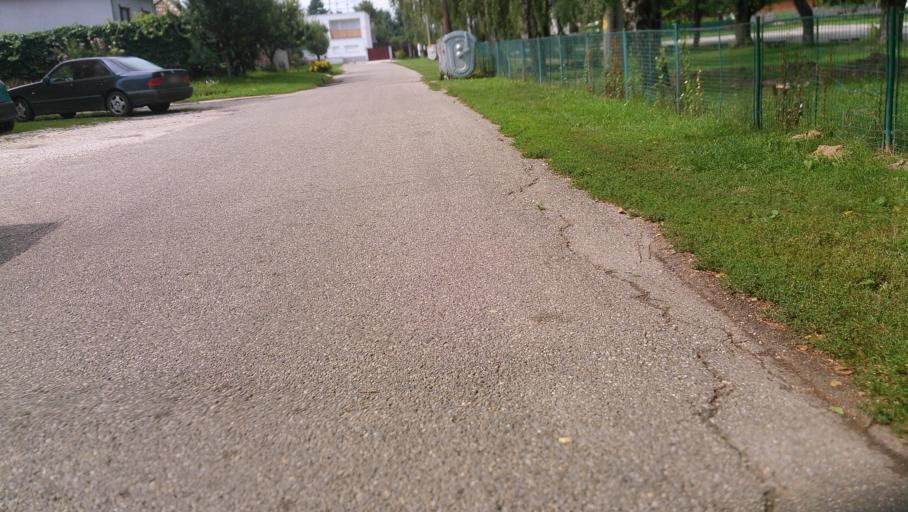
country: SK
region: Nitriansky
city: Kolarovo
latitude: 47.9137
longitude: 17.9930
